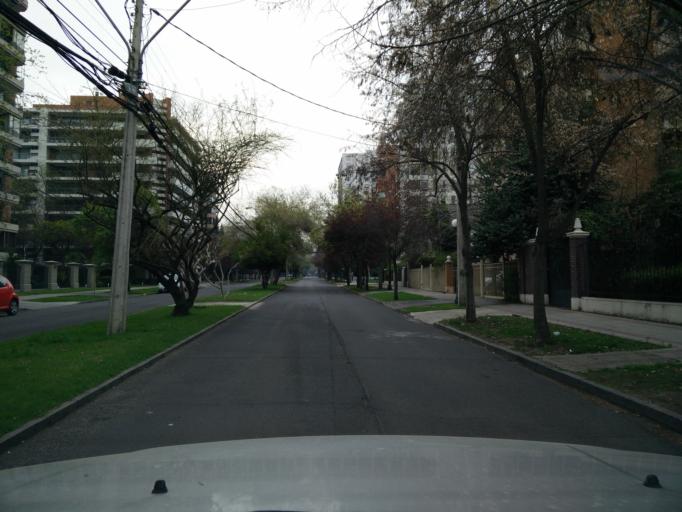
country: CL
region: Santiago Metropolitan
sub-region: Provincia de Santiago
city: Villa Presidente Frei, Nunoa, Santiago, Chile
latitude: -33.4306
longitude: -70.5951
